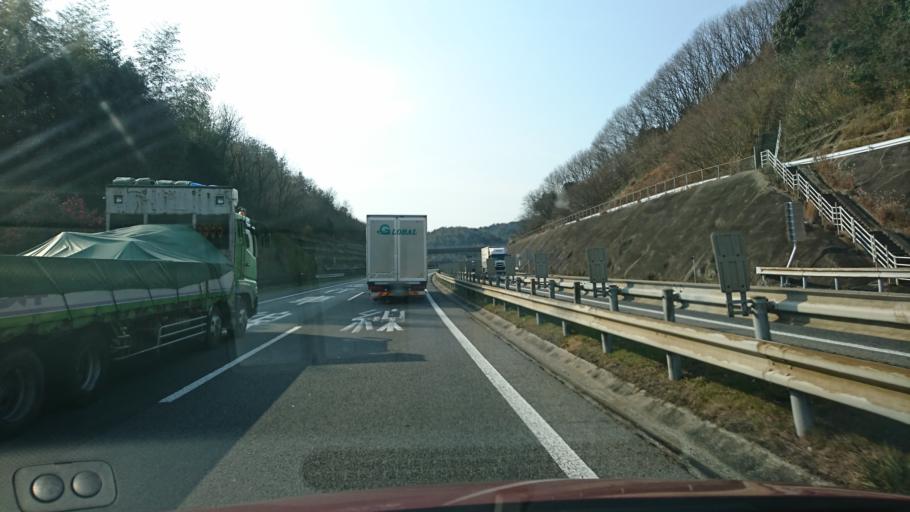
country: JP
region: Hiroshima
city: Fukuyama
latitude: 34.4848
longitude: 133.3123
